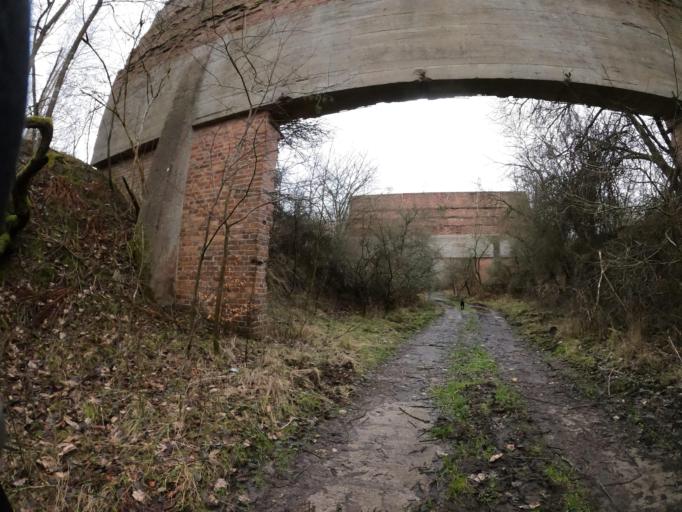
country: PL
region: Greater Poland Voivodeship
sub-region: Powiat zlotowski
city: Sypniewo
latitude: 53.4940
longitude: 16.5614
